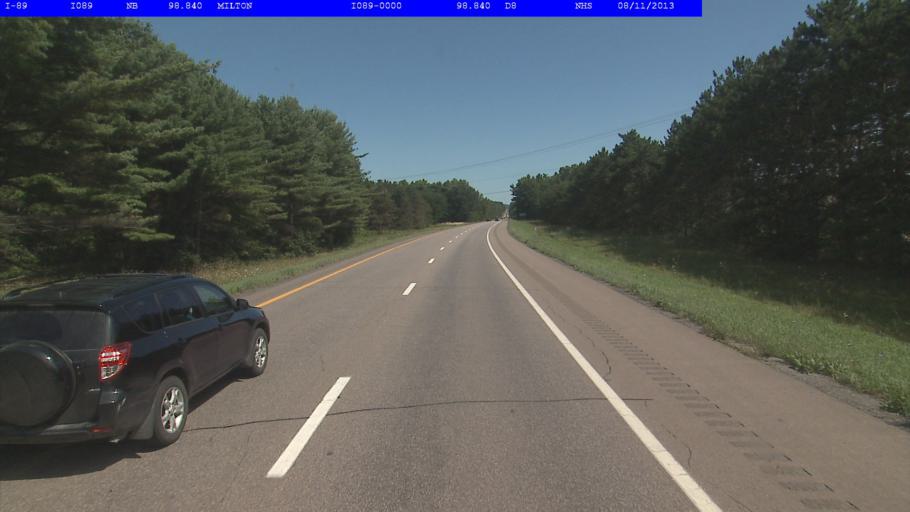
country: US
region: Vermont
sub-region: Chittenden County
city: Colchester
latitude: 44.6033
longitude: -73.1711
